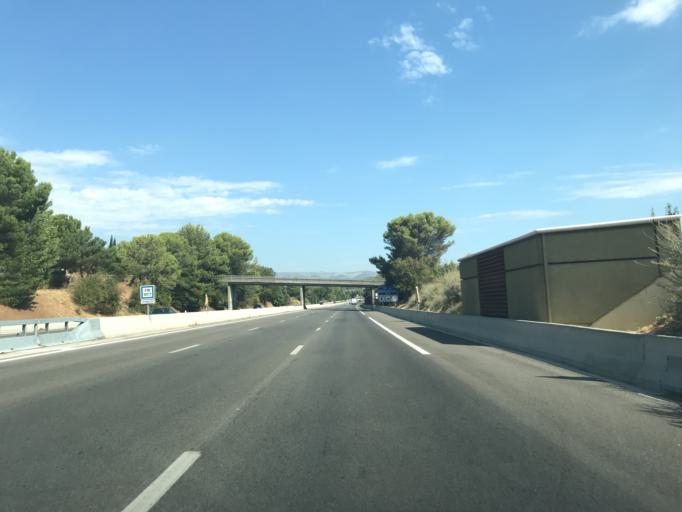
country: FR
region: Provence-Alpes-Cote d'Azur
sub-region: Departement du Var
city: Le Castellet
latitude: 43.1735
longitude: 5.7700
